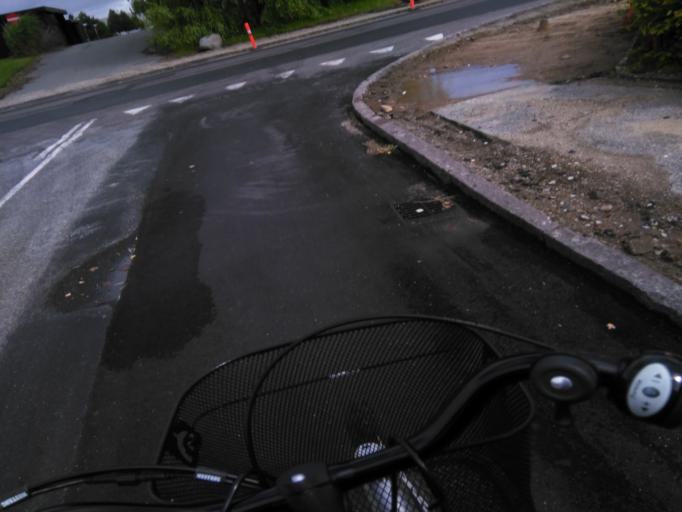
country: DK
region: Central Jutland
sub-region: Arhus Kommune
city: Marslet
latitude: 56.1078
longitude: 10.1634
